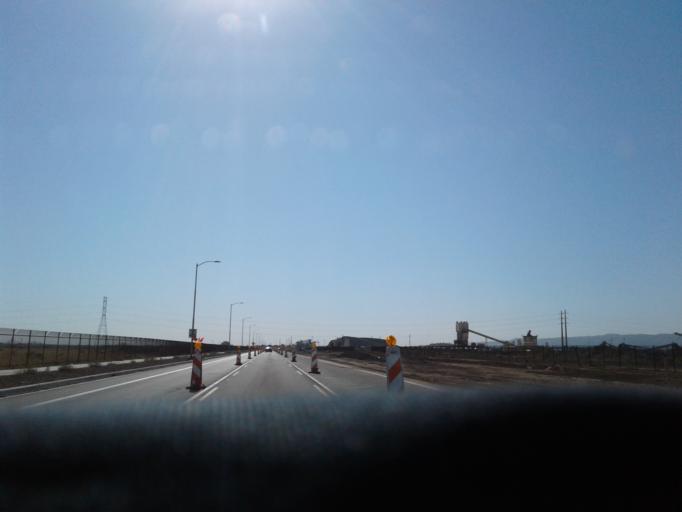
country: US
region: Arizona
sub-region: Maricopa County
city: Laveen
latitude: 33.4034
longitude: -112.1662
